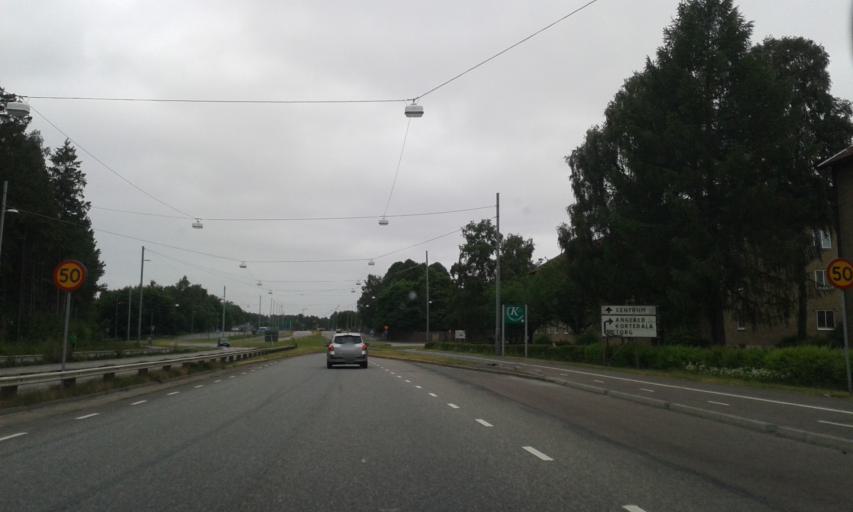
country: SE
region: Vaestra Goetaland
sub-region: Goteborg
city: Eriksbo
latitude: 57.7512
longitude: 12.0373
